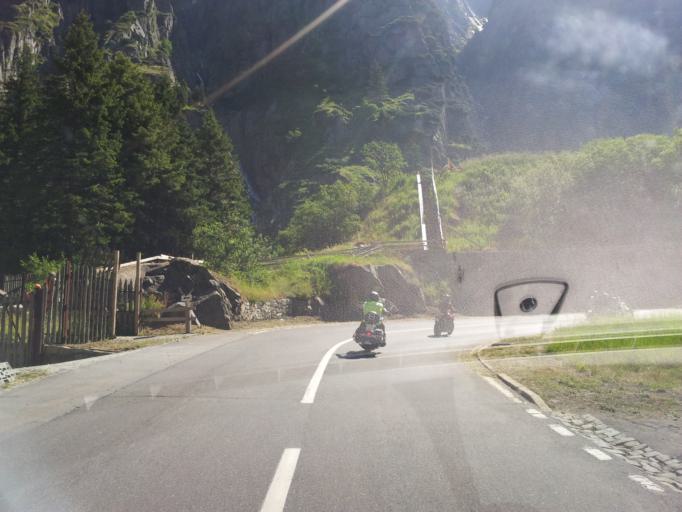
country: CH
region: Uri
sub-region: Uri
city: Andermatt
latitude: 46.6493
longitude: 8.5880
